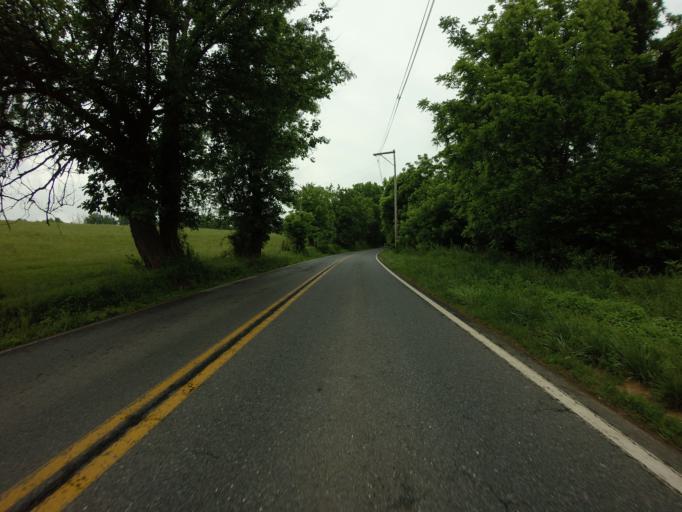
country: US
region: Maryland
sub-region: Frederick County
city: Jefferson
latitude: 39.3510
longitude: -77.5333
